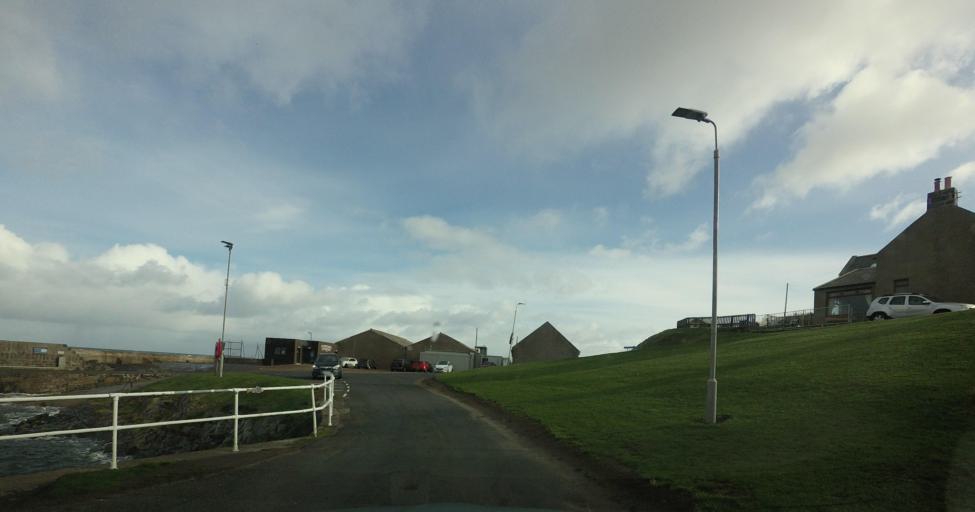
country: GB
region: Scotland
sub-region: Aberdeenshire
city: Portsoy
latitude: 57.6856
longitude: -2.6880
